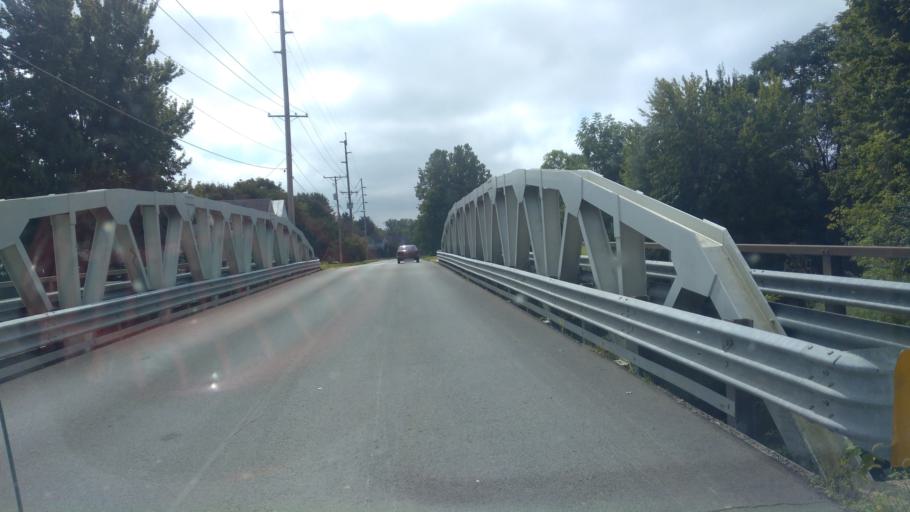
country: US
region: Ohio
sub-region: Hardin County
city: Kenton
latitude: 40.6446
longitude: -83.6135
